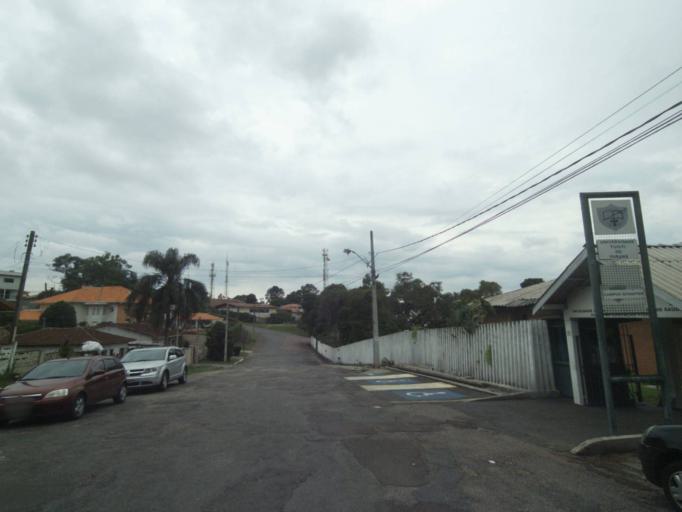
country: BR
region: Parana
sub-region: Curitiba
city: Curitiba
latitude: -25.4007
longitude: -49.2892
